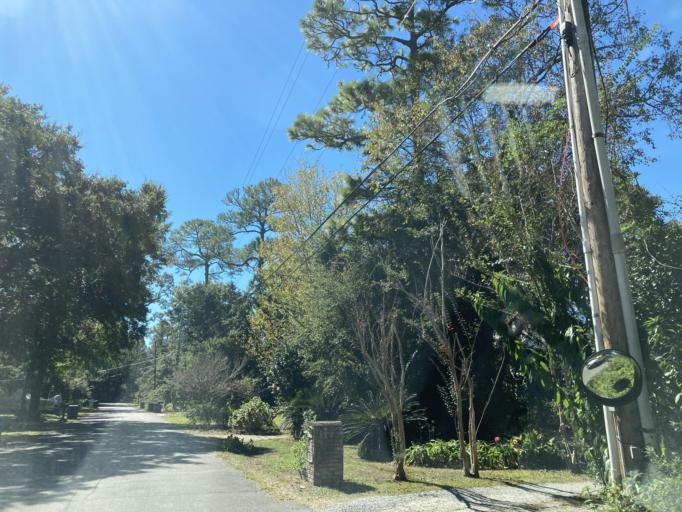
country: US
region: Mississippi
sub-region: Jackson County
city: Ocean Springs
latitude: 30.4053
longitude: -88.8174
